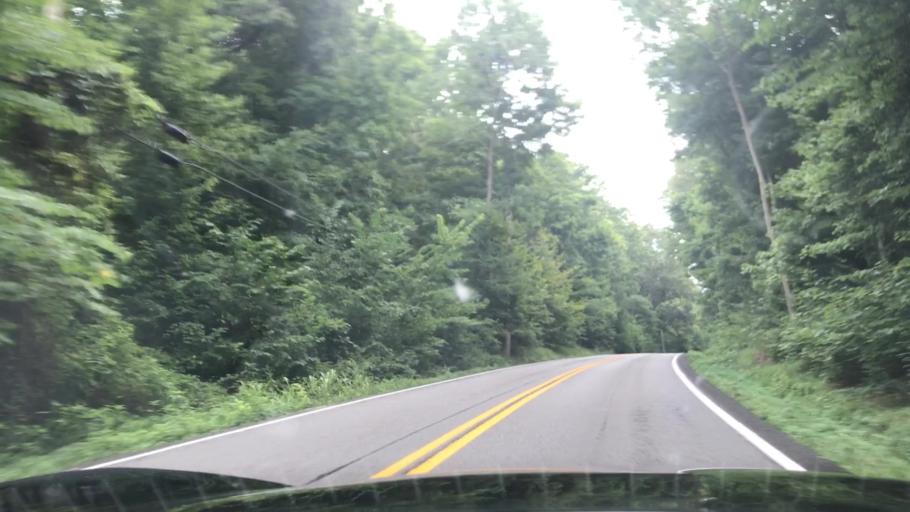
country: US
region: Kentucky
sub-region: Muhlenberg County
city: Central City
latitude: 37.2005
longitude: -87.0288
